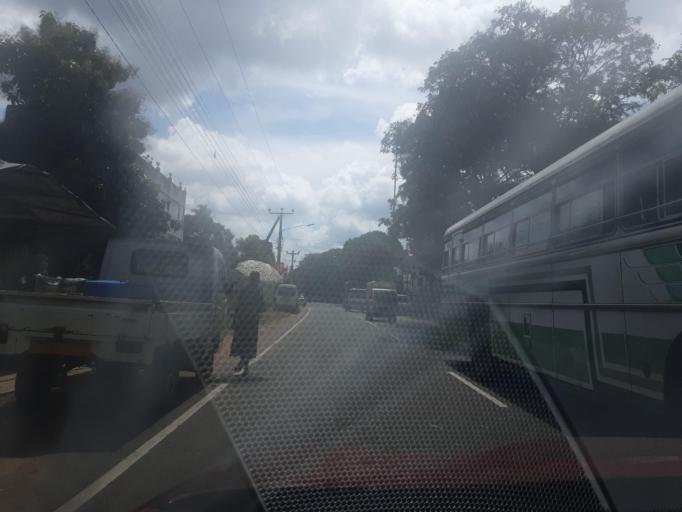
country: LK
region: North Western
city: Kuliyapitiya
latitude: 7.4700
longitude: 80.0482
